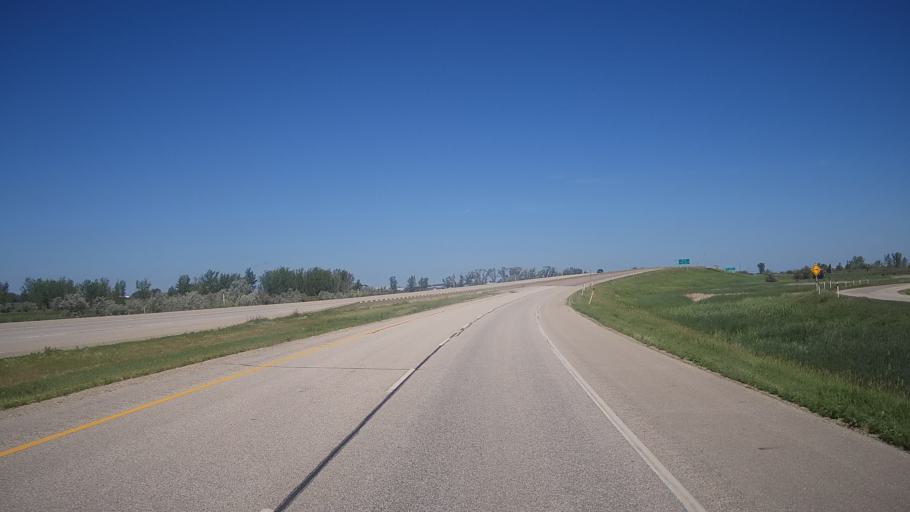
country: CA
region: Manitoba
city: Portage la Prairie
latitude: 49.9634
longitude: -98.3535
